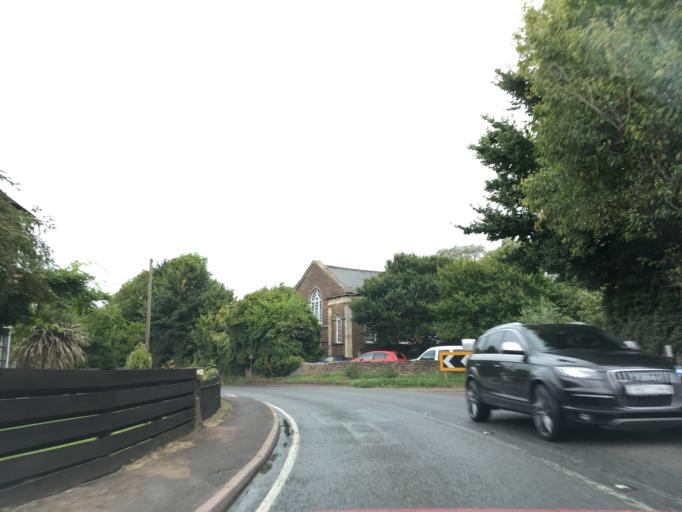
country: GB
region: England
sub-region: Herefordshire
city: Lea
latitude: 51.9003
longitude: -2.5233
